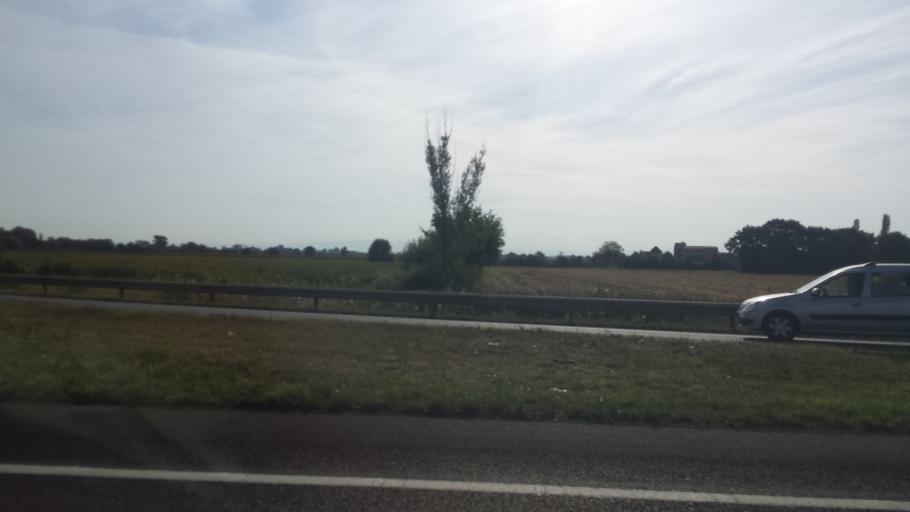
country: FR
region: Auvergne
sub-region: Departement du Puy-de-Dome
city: Menetrol
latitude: 45.8929
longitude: 3.1536
